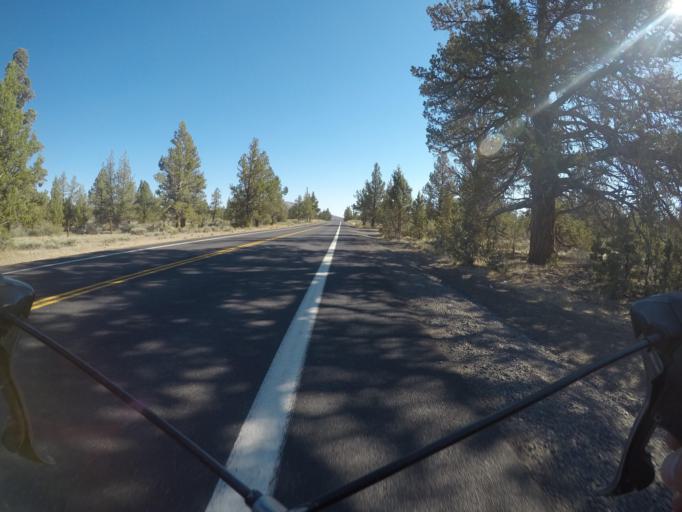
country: US
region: Oregon
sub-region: Deschutes County
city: Redmond
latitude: 44.2197
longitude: -121.3126
